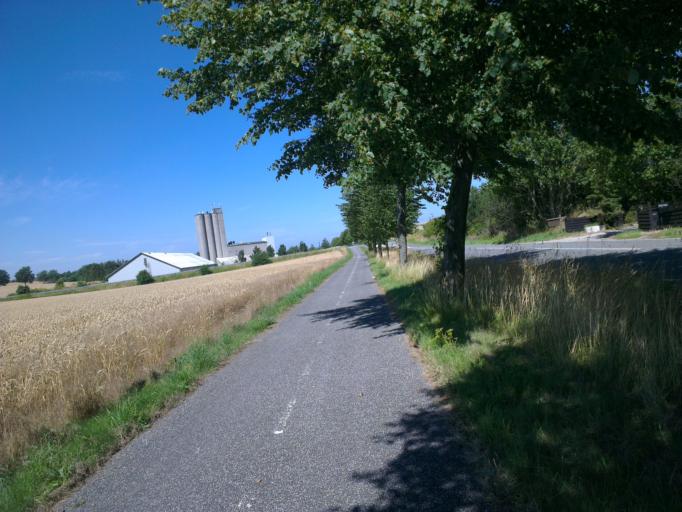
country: DK
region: Capital Region
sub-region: Frederikssund Kommune
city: Slangerup
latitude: 55.8310
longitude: 12.1861
